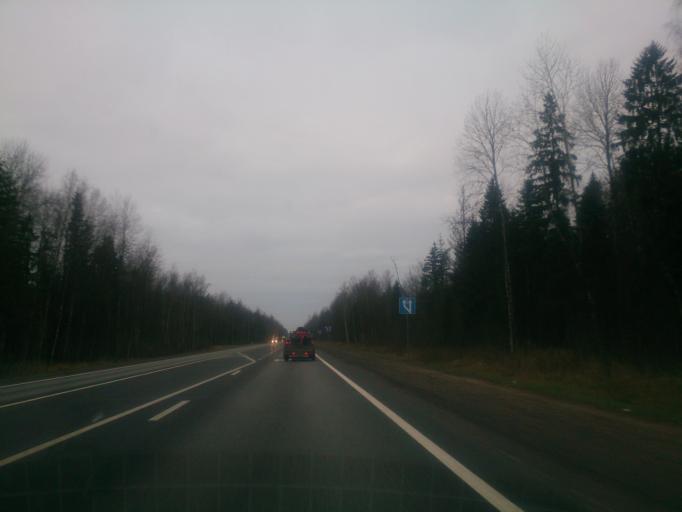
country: RU
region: Novgorod
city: Proletariy
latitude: 58.3900
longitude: 31.9361
